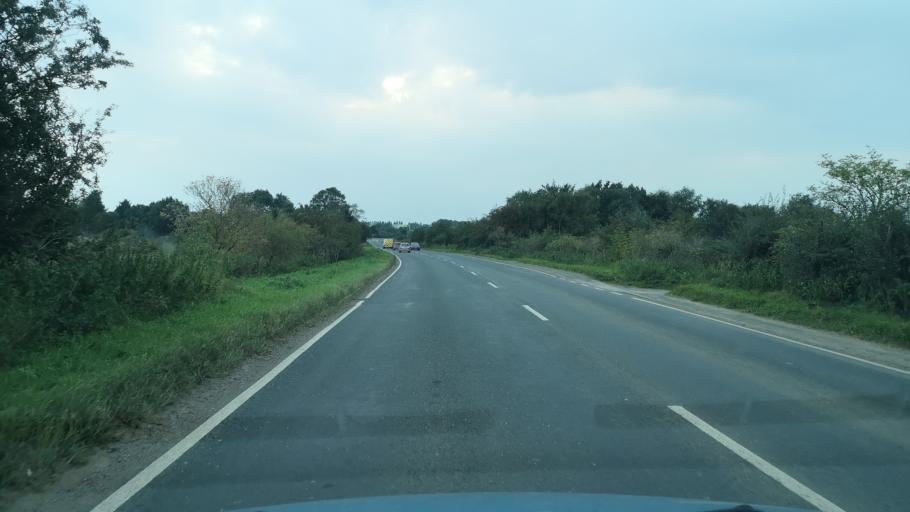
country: GB
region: England
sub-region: East Riding of Yorkshire
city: Snaith
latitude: 53.6849
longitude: -1.0507
